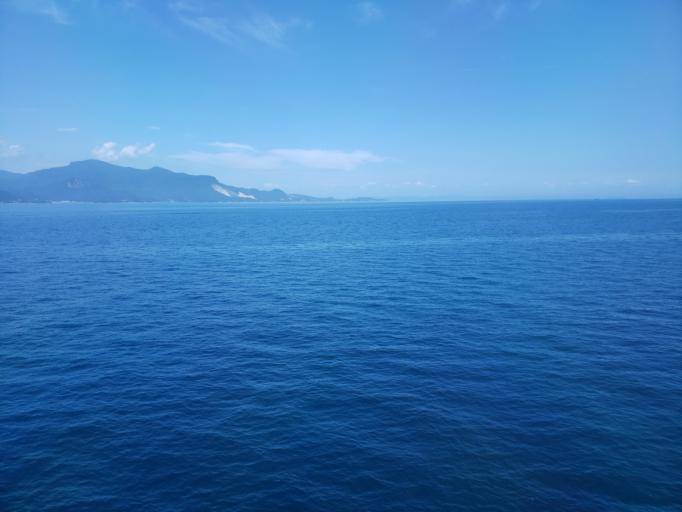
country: JP
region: Kagawa
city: Tonosho
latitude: 34.4421
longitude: 134.4043
